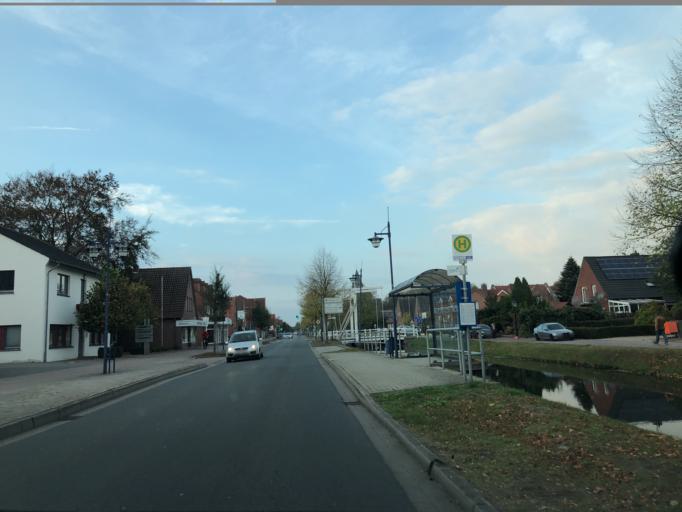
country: DE
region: Lower Saxony
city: Papenburg
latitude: 53.0699
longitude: 7.4447
